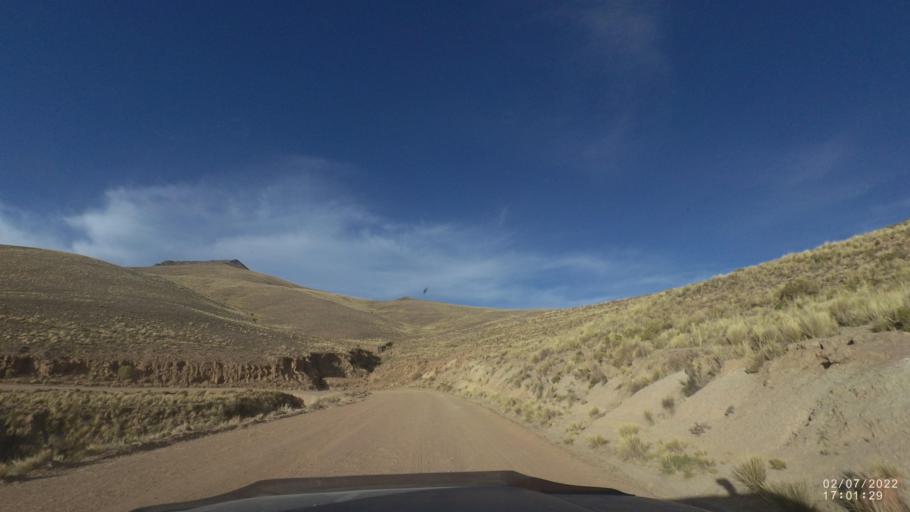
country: BO
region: Cochabamba
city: Irpa Irpa
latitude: -17.9316
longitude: -66.5542
